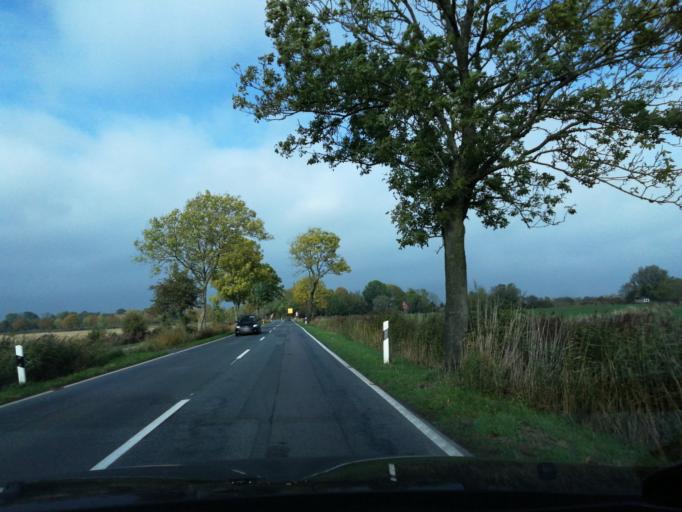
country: DE
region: Lower Saxony
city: Fedderwarden
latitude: 53.6205
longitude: 8.0349
